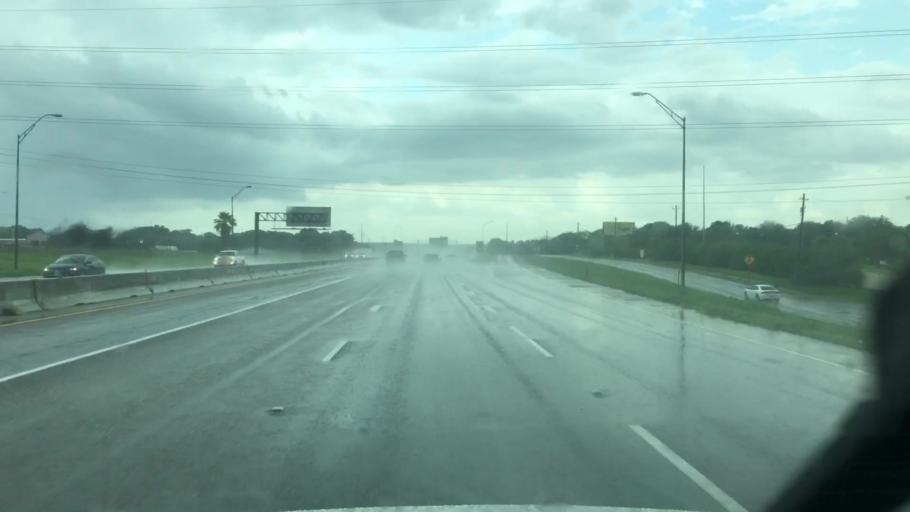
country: US
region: Texas
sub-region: Nueces County
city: Robstown
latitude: 27.8578
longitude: -97.6041
